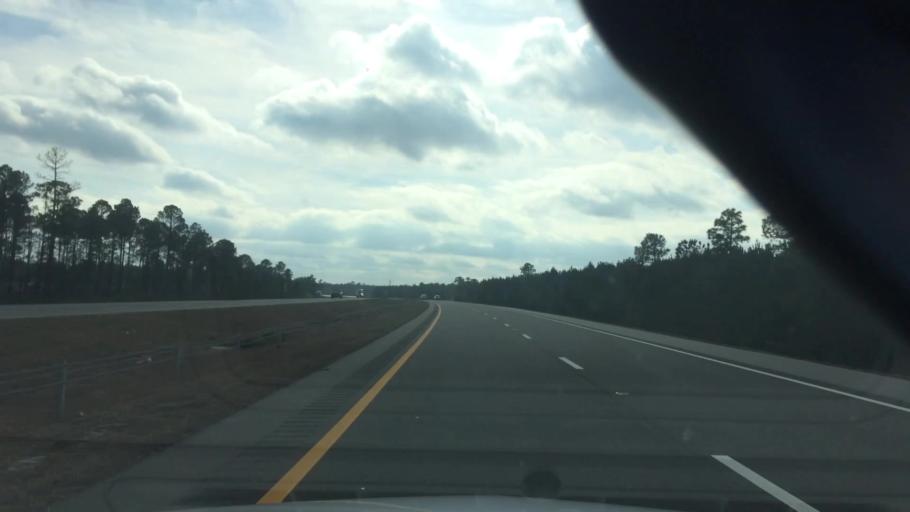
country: US
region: North Carolina
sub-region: Brunswick County
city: Leland
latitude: 34.2705
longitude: -78.0771
